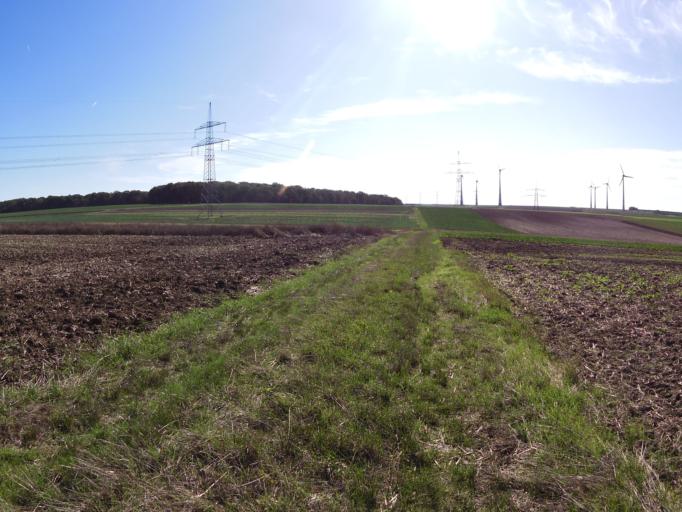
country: DE
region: Bavaria
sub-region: Regierungsbezirk Unterfranken
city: Theilheim
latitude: 49.7366
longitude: 10.0469
